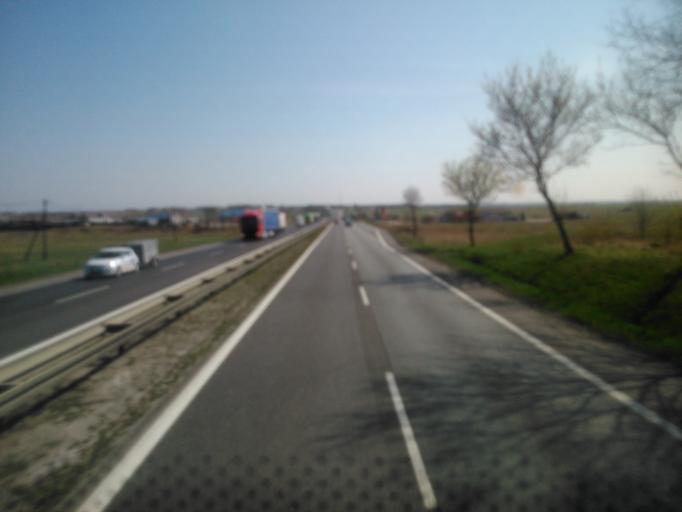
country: PL
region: Silesian Voivodeship
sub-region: Powiat myszkowski
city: Kozieglowy
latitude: 50.6246
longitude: 19.1435
